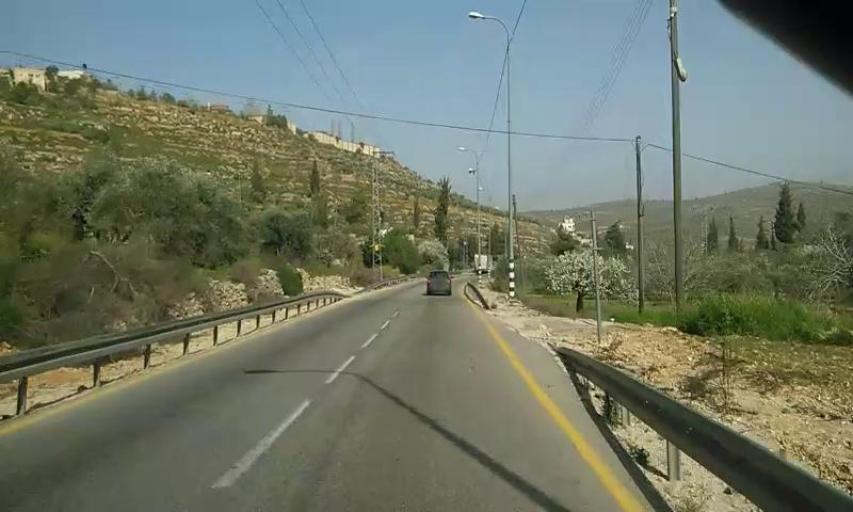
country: PS
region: West Bank
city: Sinjil
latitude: 32.0341
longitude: 35.2714
